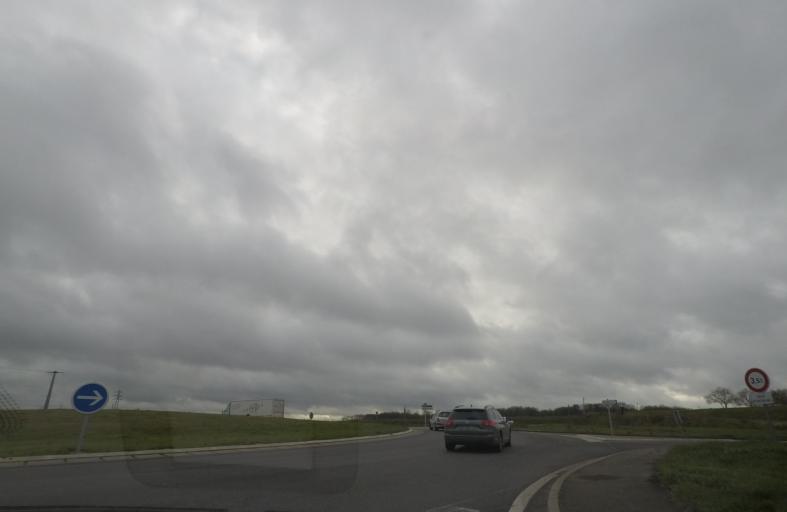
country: FR
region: Centre
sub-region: Departement du Loir-et-Cher
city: Vendome
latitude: 47.7720
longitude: 1.0591
